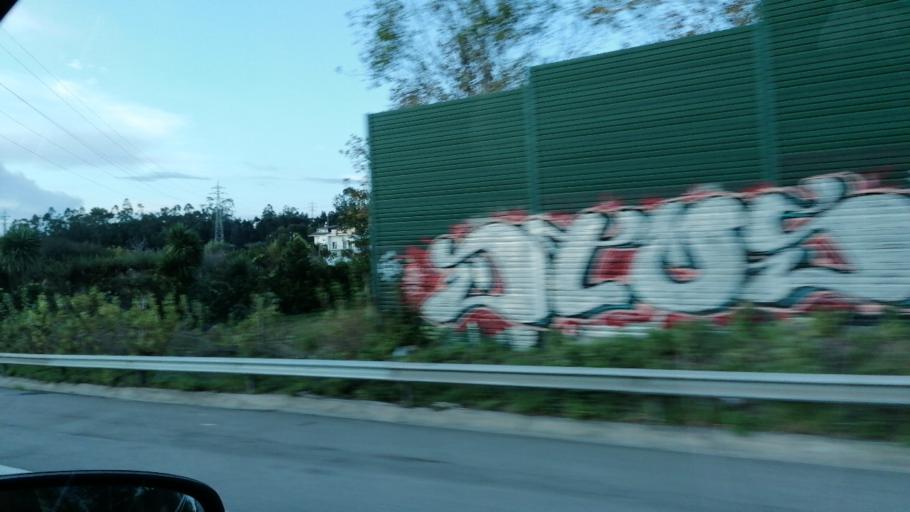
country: PT
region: Porto
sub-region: Matosinhos
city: Guifoes
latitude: 41.1903
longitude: -8.6769
